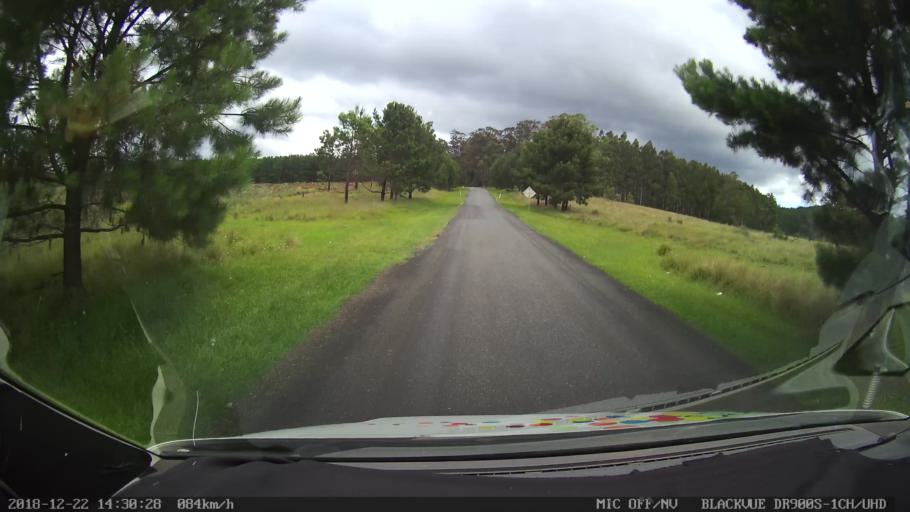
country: AU
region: New South Wales
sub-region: Bellingen
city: Dorrigo
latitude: -30.0869
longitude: 152.6315
